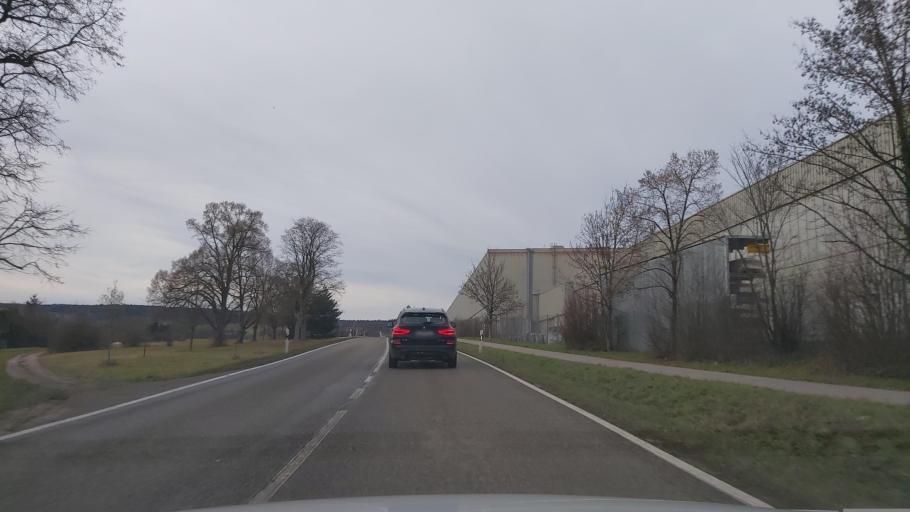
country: DE
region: Baden-Wuerttemberg
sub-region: Tuebingen Region
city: Ehingen
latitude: 48.2934
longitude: 9.7095
